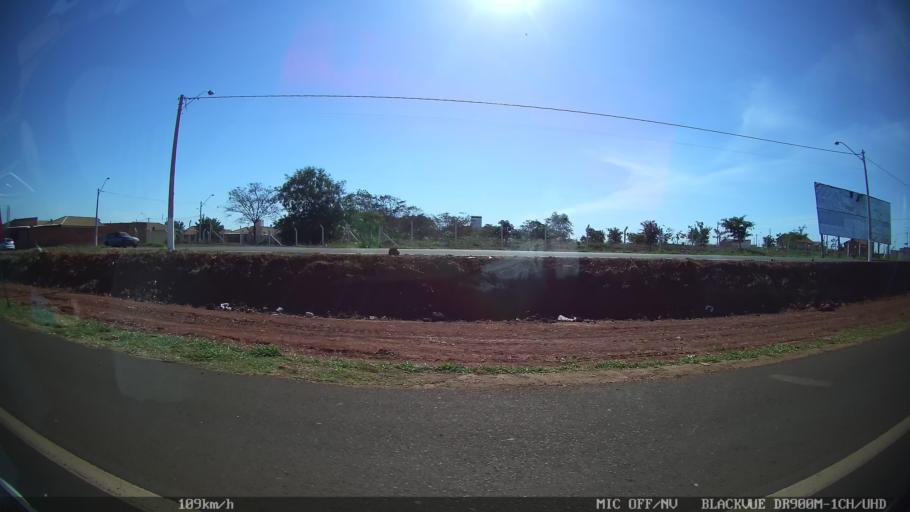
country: BR
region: Sao Paulo
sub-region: Olimpia
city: Olimpia
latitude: -20.7330
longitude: -48.8726
